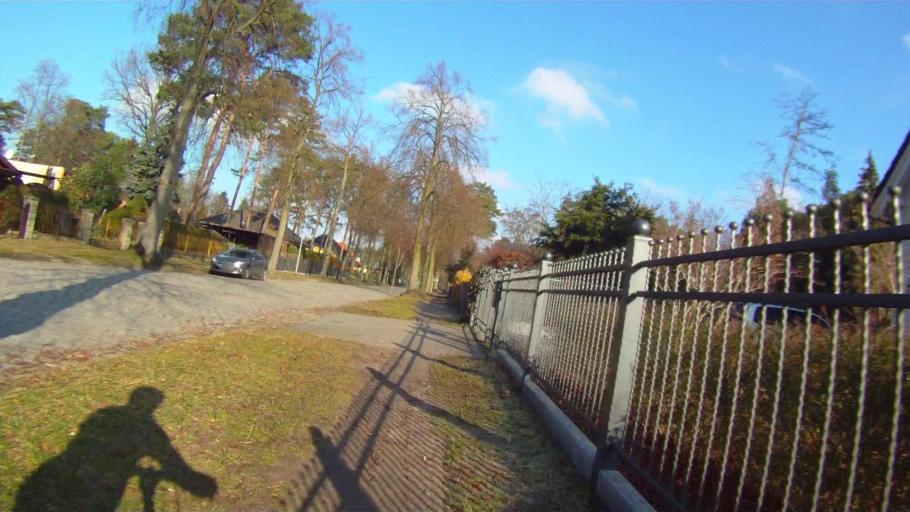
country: DE
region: Brandenburg
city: Schoneiche
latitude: 52.4680
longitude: 13.7157
